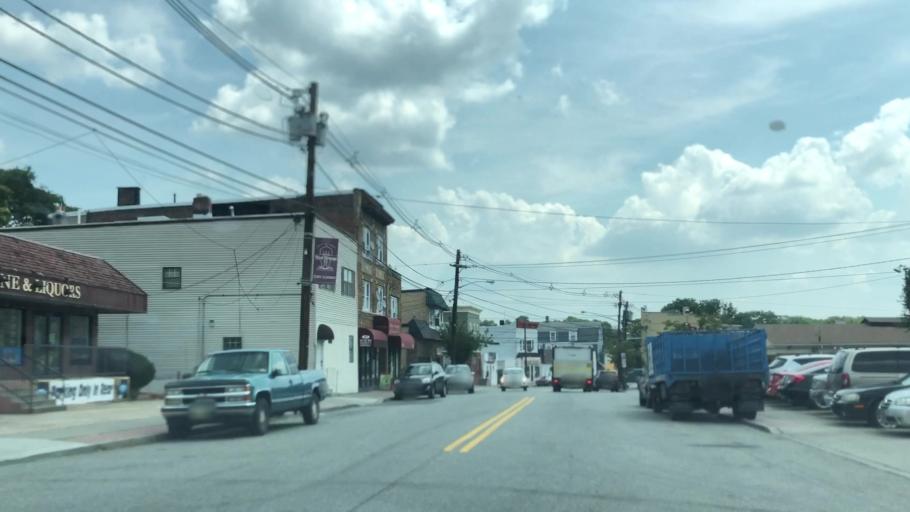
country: US
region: New Jersey
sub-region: Essex County
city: Orange
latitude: 40.7863
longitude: -74.2288
